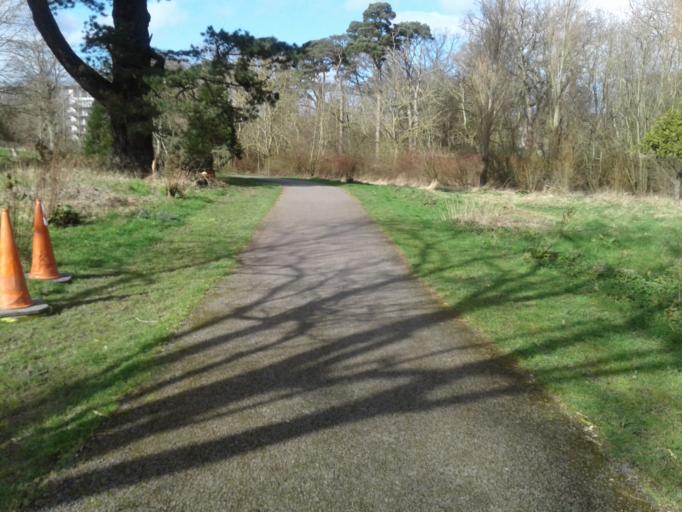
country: IE
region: Leinster
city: Beaumont
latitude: 53.4033
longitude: -6.2489
